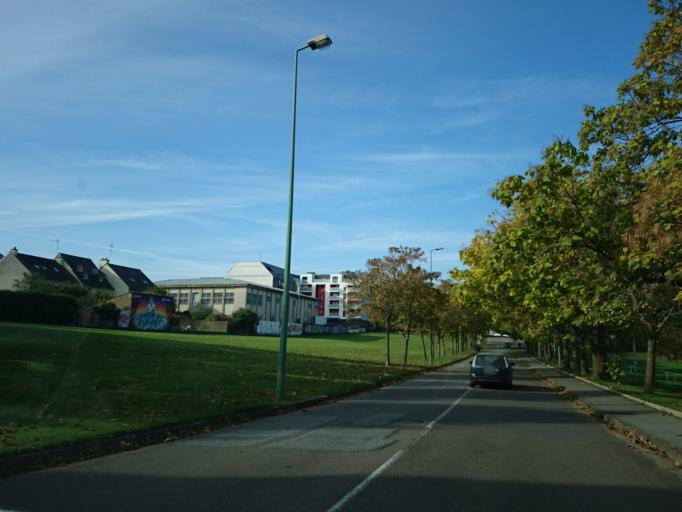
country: FR
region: Brittany
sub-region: Departement d'Ille-et-Vilaine
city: Rennes
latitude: 48.1176
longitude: -1.6477
